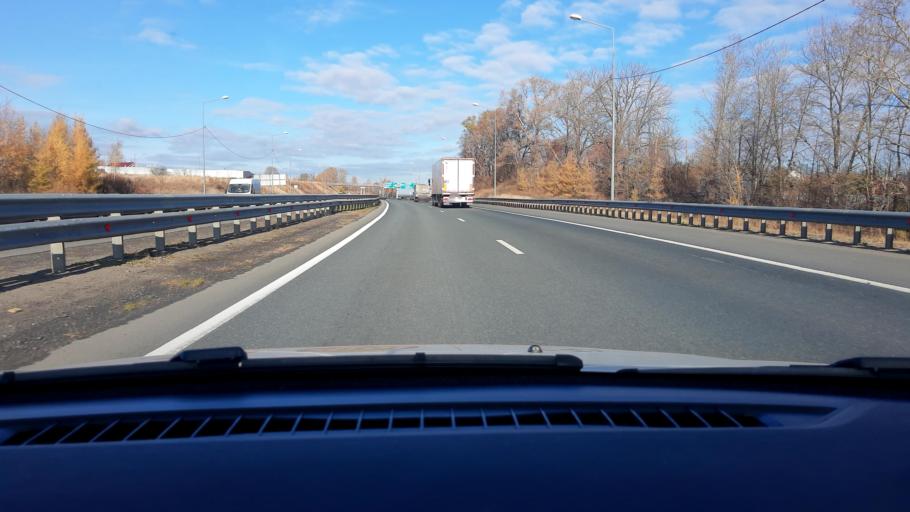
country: RU
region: Nizjnij Novgorod
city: Burevestnik
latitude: 56.1657
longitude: 43.7498
